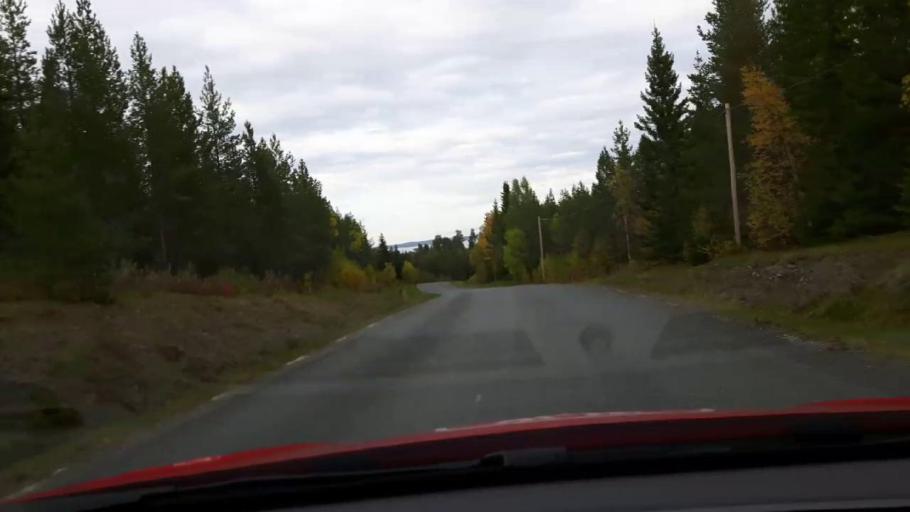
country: SE
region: Jaemtland
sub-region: Krokoms Kommun
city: Krokom
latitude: 63.2196
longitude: 14.1267
